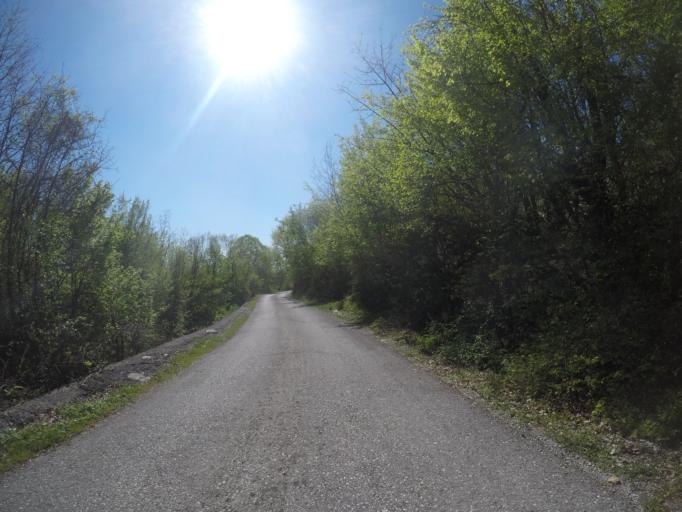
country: ME
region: Danilovgrad
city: Danilovgrad
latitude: 42.5165
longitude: 19.0533
